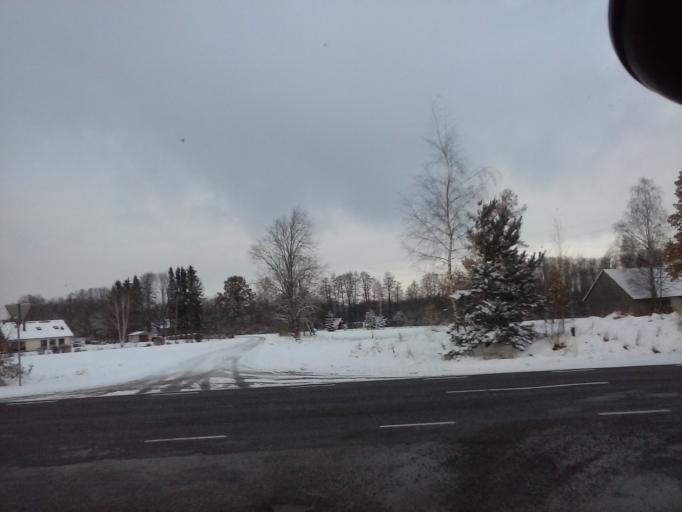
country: EE
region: Tartu
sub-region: UElenurme vald
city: Ulenurme
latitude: 58.3228
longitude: 26.8159
